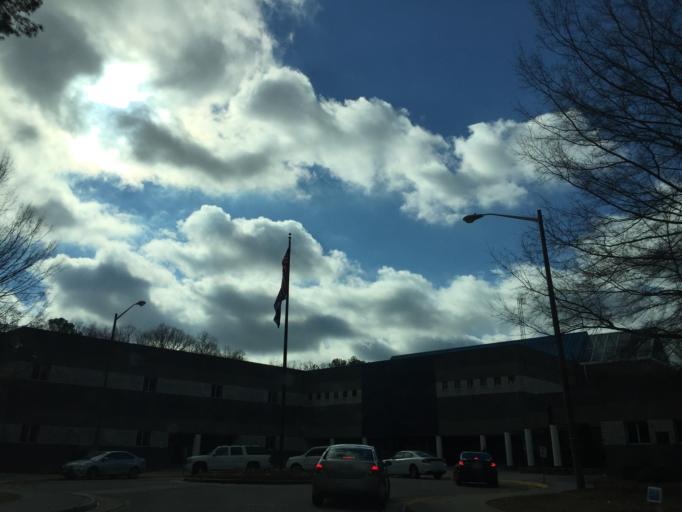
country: US
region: Virginia
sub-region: City of Newport News
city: Newport News
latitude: 37.0722
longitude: -76.4998
